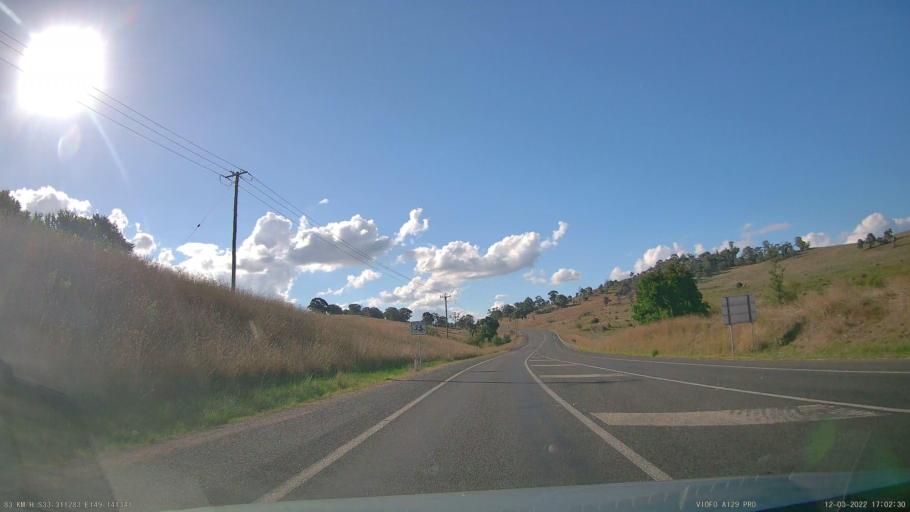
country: AU
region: New South Wales
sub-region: Orange Municipality
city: Orange
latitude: -33.3111
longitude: 149.1413
